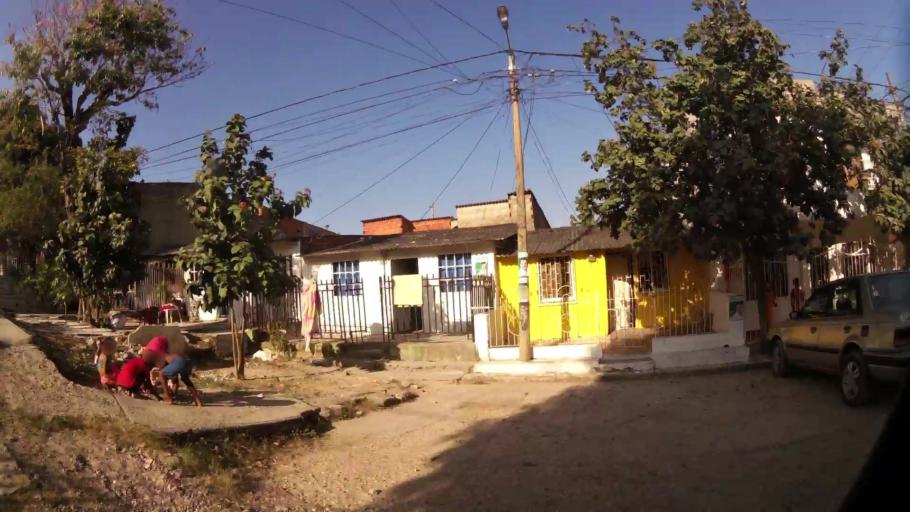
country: CO
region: Bolivar
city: Cartagena
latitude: 10.4018
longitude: -75.4796
